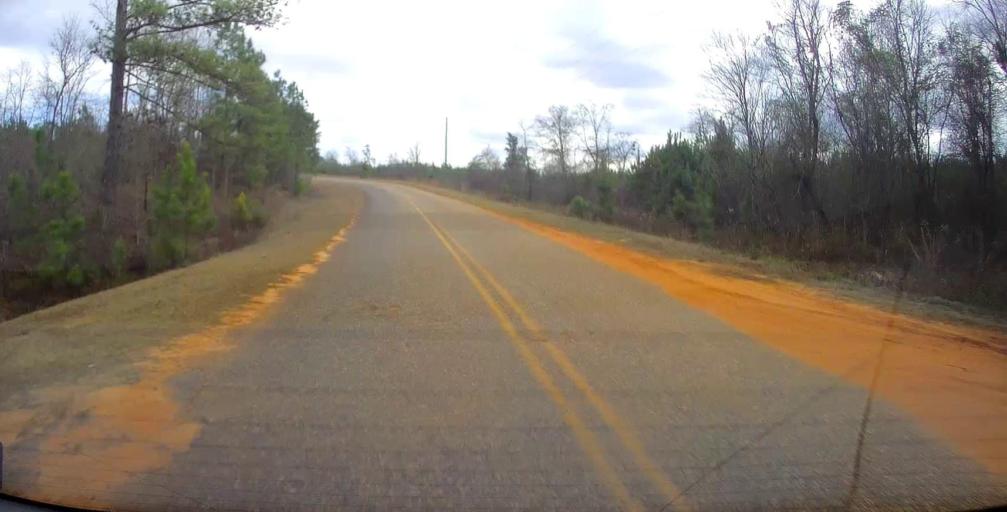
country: US
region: Georgia
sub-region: Marion County
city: Buena Vista
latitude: 32.4270
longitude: -84.4192
